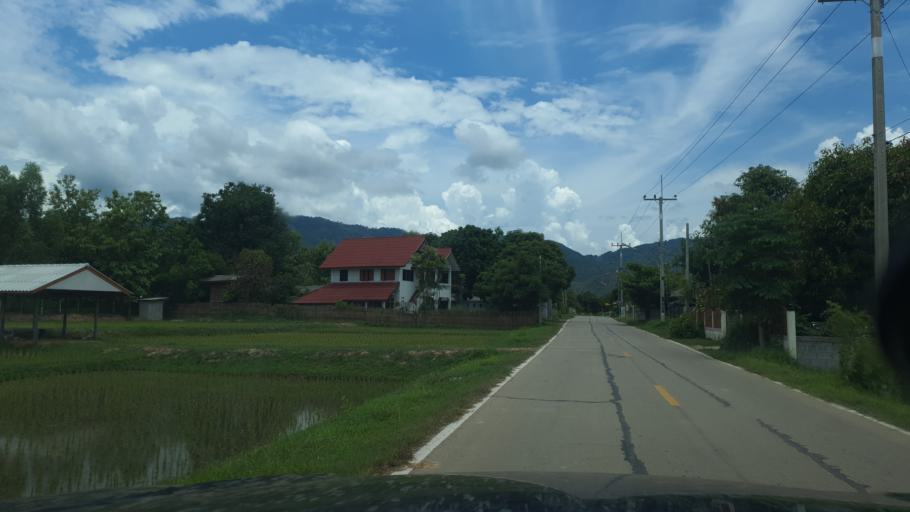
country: TH
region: Lampang
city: Sop Prap
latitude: 17.9126
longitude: 99.4125
